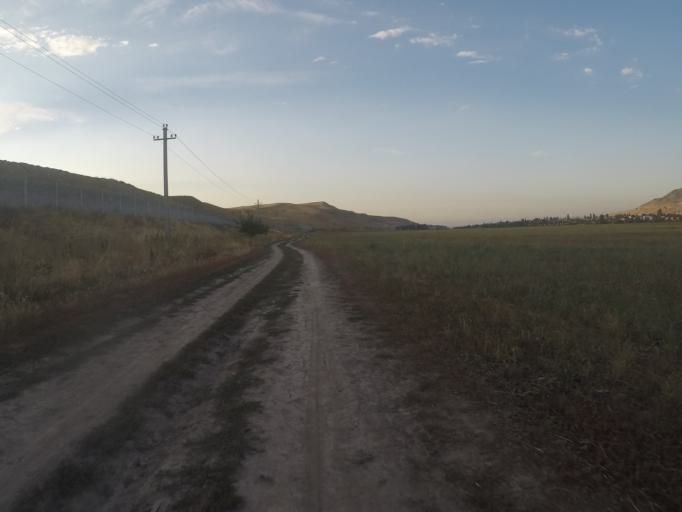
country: KG
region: Chuy
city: Bishkek
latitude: 42.7550
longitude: 74.6364
